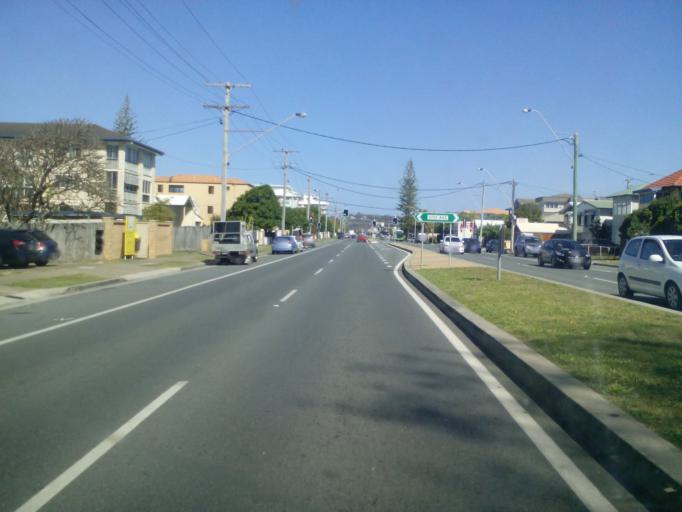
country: AU
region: Queensland
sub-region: Gold Coast
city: Palm Beach
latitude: -28.1147
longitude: 153.4688
